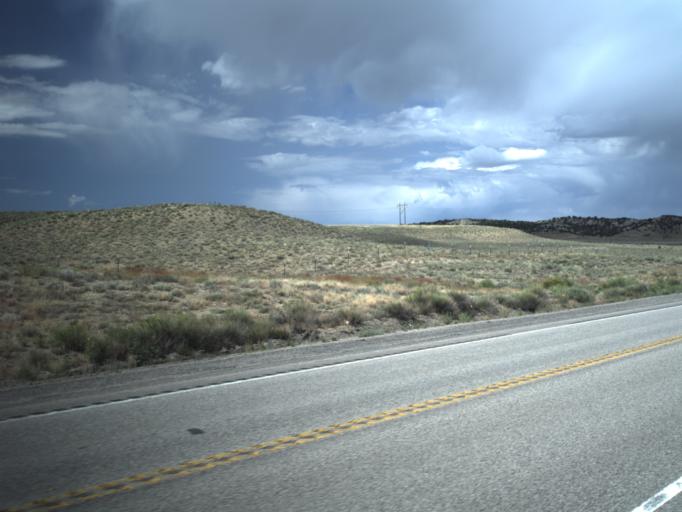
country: US
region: Utah
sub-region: Carbon County
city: Wellington
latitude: 39.5399
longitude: -110.6061
